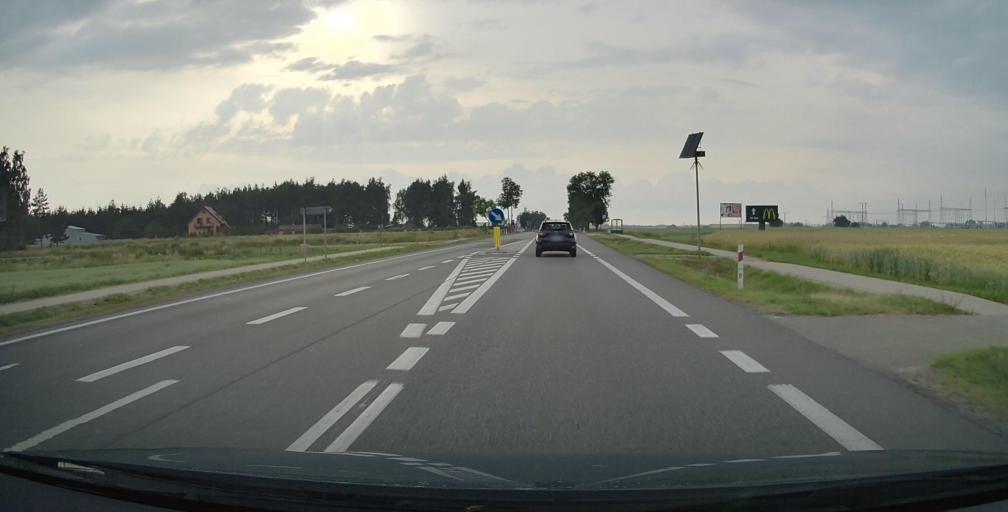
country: PL
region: Masovian Voivodeship
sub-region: Siedlce
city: Siedlce
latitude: 52.1247
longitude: 22.3471
